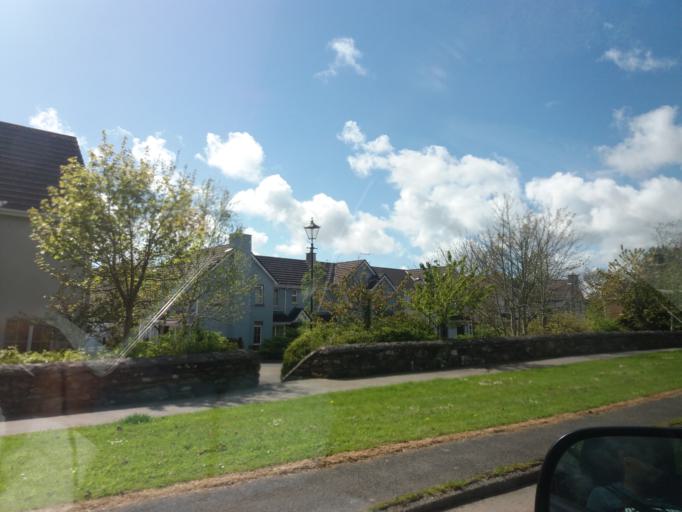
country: IE
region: Munster
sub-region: Waterford
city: Waterford
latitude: 52.2394
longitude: -7.0655
